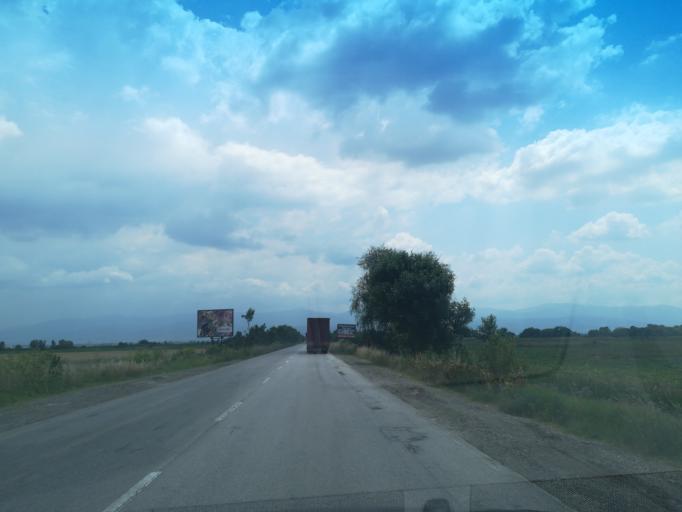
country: BG
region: Plovdiv
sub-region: Obshtina Plovdiv
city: Plovdiv
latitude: 42.1822
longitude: 24.6765
